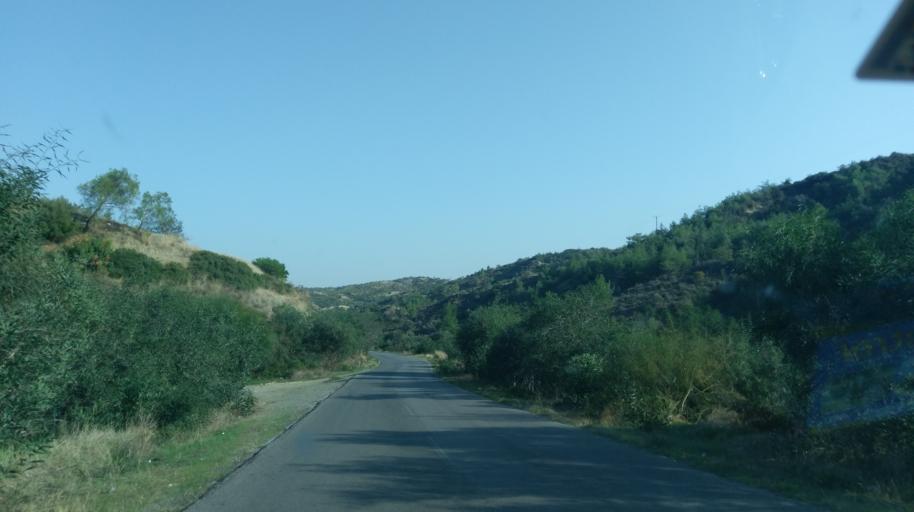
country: CY
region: Lefkosia
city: Lefka
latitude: 35.1530
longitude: 32.7761
